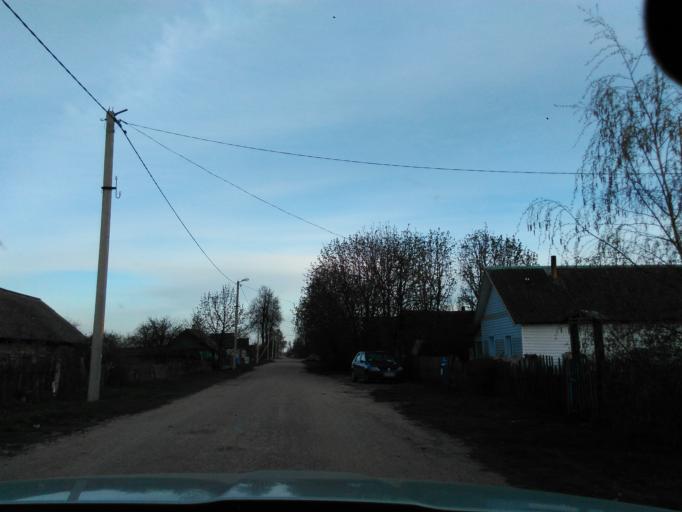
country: BY
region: Vitebsk
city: Chashniki
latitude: 54.8537
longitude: 29.1716
